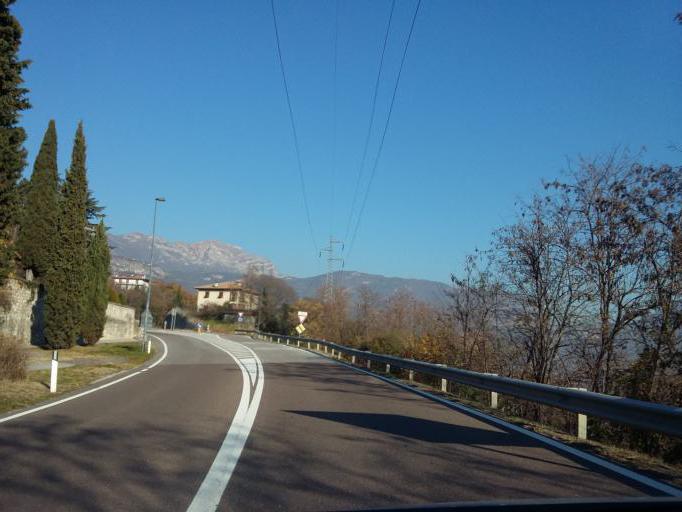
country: IT
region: Trentino-Alto Adige
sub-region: Provincia di Trento
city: Isera
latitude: 45.8886
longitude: 11.0127
